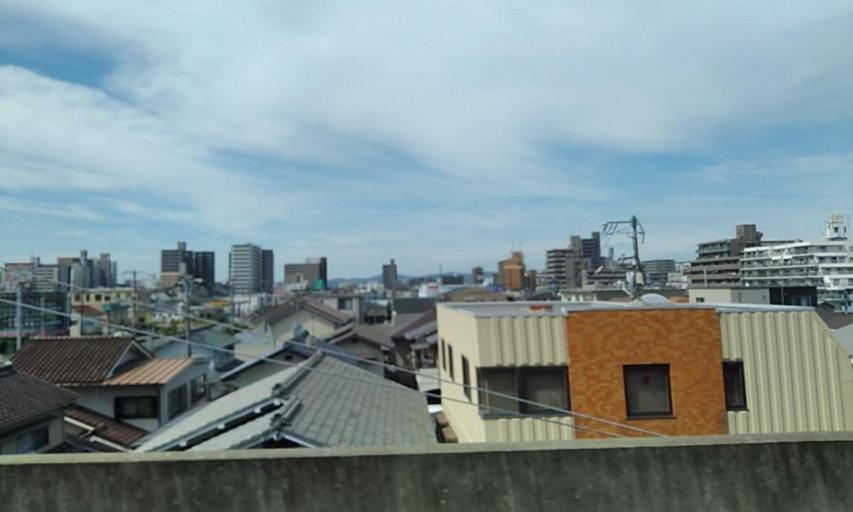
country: JP
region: Okayama
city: Okayama-shi
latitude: 34.6512
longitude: 133.9106
